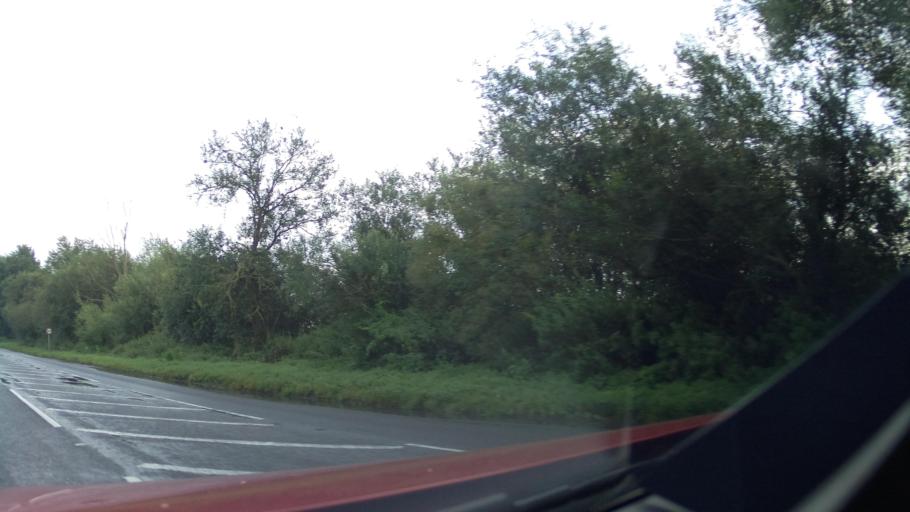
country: GB
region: England
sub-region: Oxfordshire
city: Kidlington
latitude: 51.8349
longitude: -1.3046
